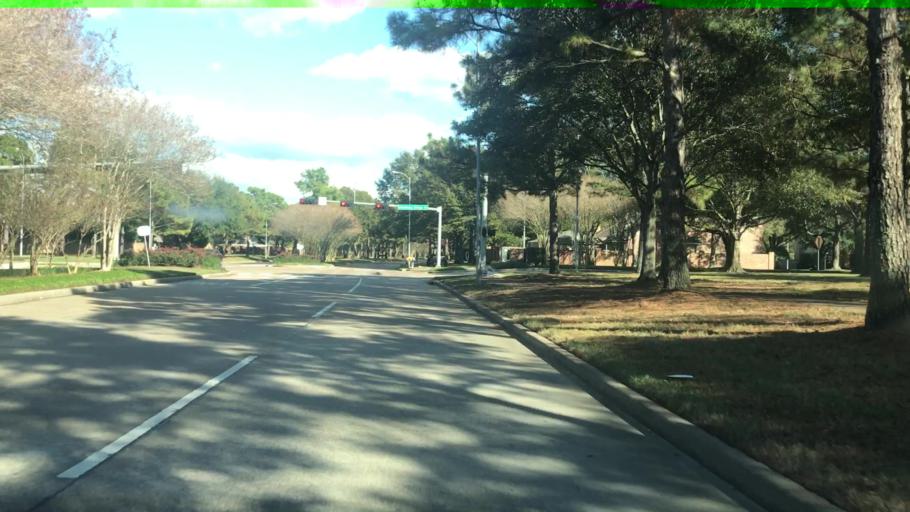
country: US
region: Texas
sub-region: Fort Bend County
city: Cinco Ranch
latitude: 29.7567
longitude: -95.7739
